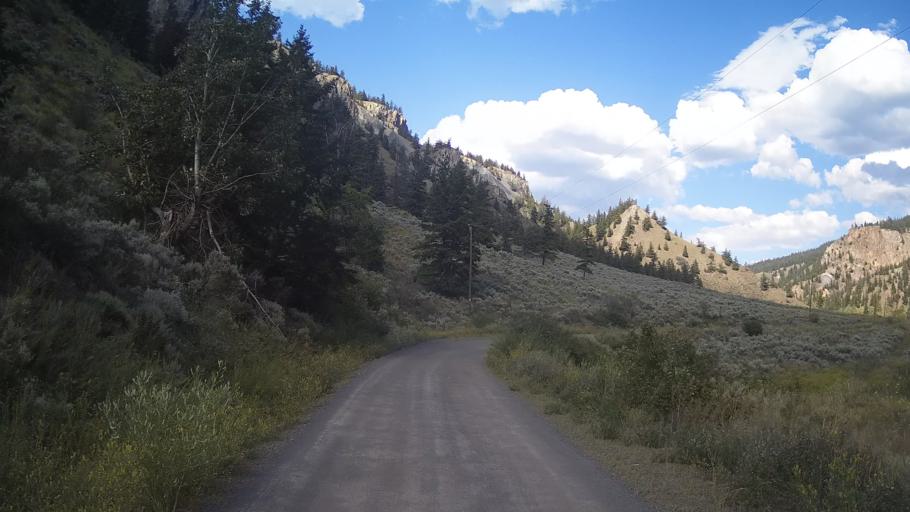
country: CA
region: British Columbia
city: Lillooet
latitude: 51.2225
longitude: -122.0725
